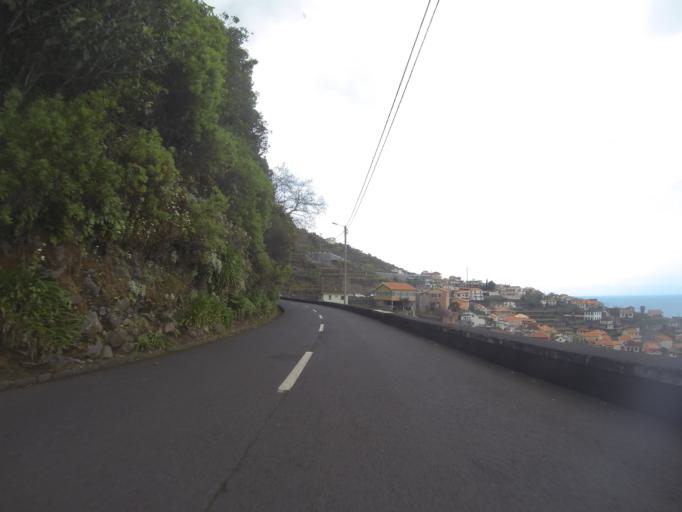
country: PT
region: Madeira
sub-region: Sao Vicente
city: Sao Vicente
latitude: 32.8215
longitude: -17.1056
